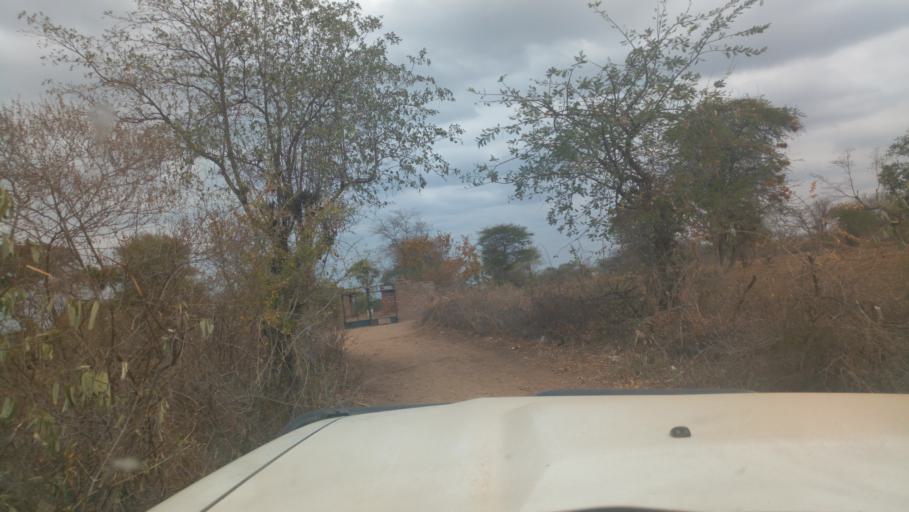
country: KE
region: Kitui
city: Kitui
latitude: -1.5882
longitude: 37.9283
